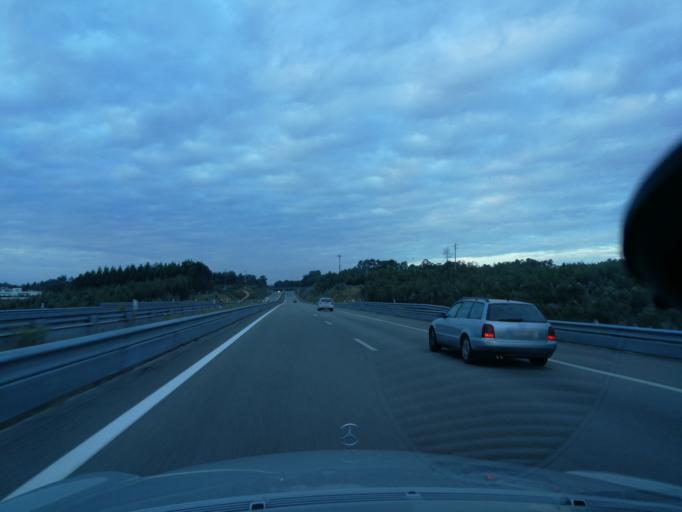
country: PT
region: Aveiro
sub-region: Estarreja
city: Salreu
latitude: 40.7122
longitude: -8.5328
